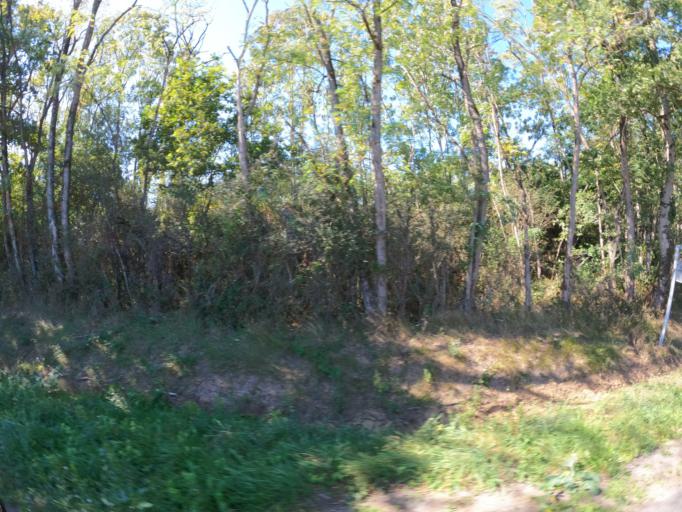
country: FR
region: Poitou-Charentes
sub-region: Departement de la Vienne
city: Lathus-Saint-Remy
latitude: 46.3644
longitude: 0.9395
